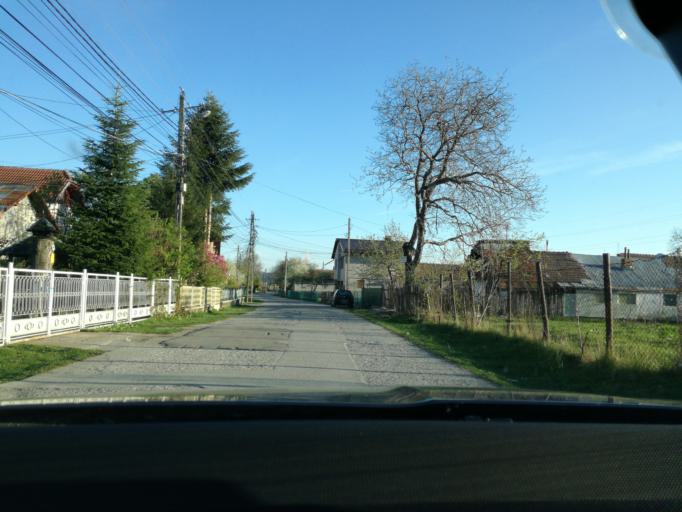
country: RO
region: Prahova
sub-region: Comuna Cornu
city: Cornu de Jos
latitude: 45.1497
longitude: 25.7014
